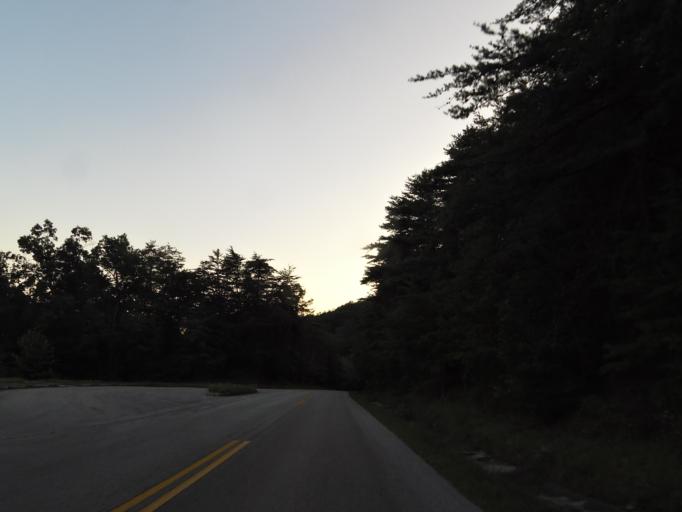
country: US
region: Tennessee
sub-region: Blount County
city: Maryville
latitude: 35.6125
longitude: -83.9734
